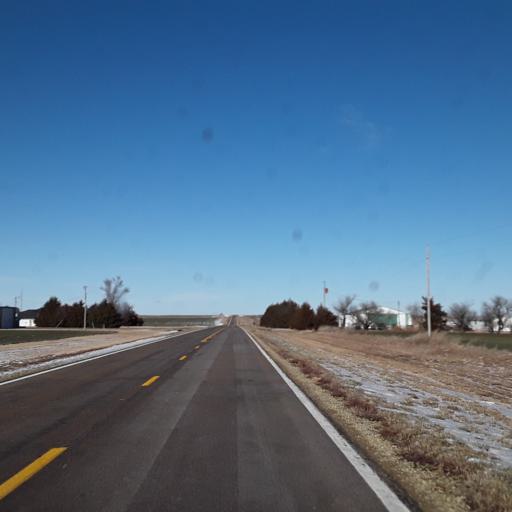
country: US
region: Kansas
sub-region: Mitchell County
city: Beloit
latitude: 39.3558
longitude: -98.1161
